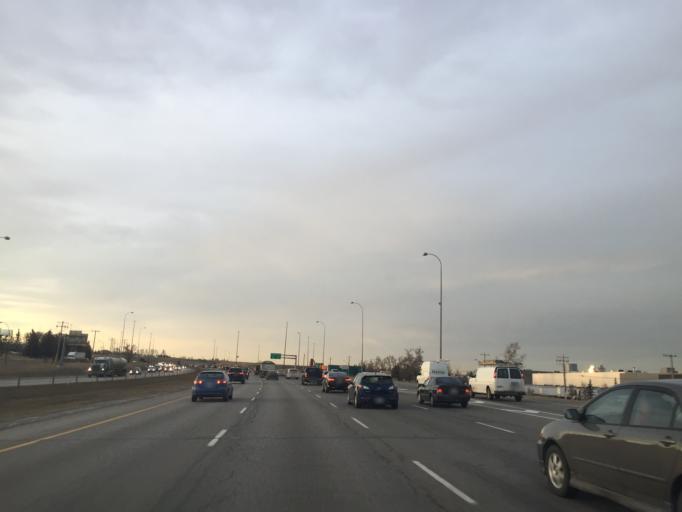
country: CA
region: Alberta
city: Calgary
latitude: 51.1026
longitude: -114.0457
